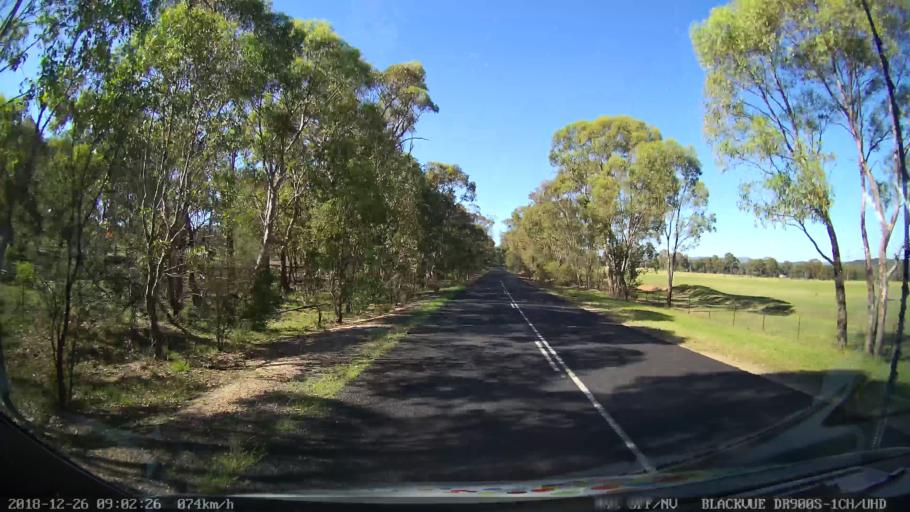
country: AU
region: New South Wales
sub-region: Mid-Western Regional
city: Kandos
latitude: -32.6528
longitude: 150.0190
